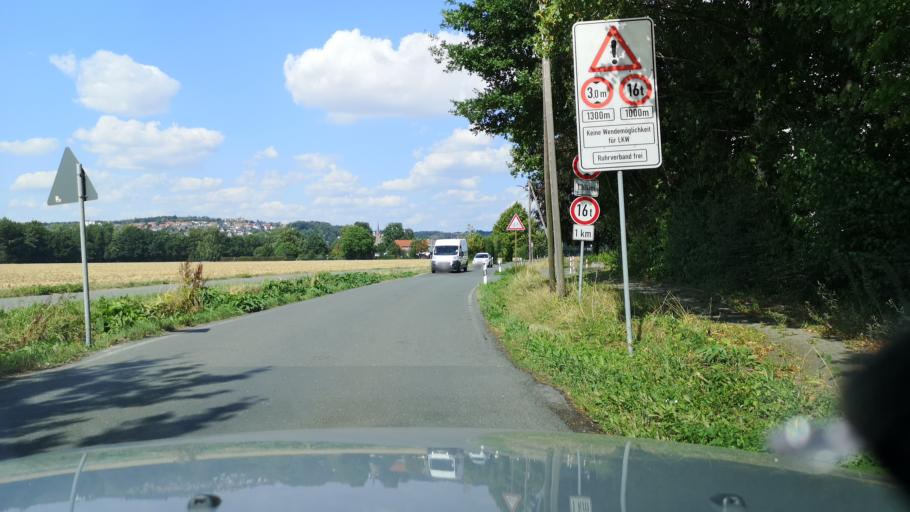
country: DE
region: North Rhine-Westphalia
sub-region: Regierungsbezirk Arnsberg
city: Frondenberg
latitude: 51.4592
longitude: 7.7592
